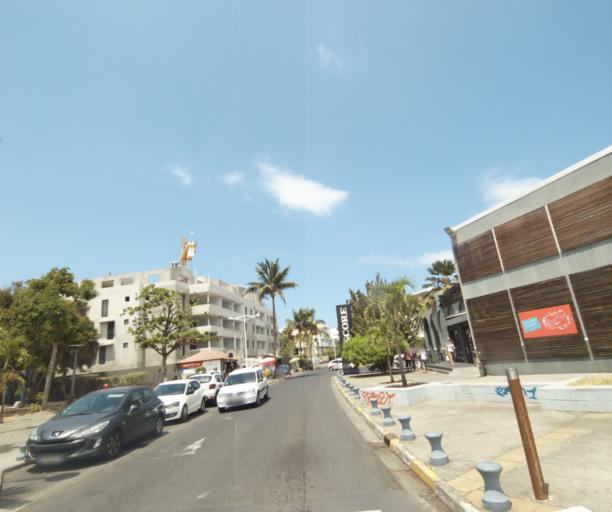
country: RE
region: Reunion
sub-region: Reunion
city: Saint-Paul
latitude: -21.0737
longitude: 55.2233
